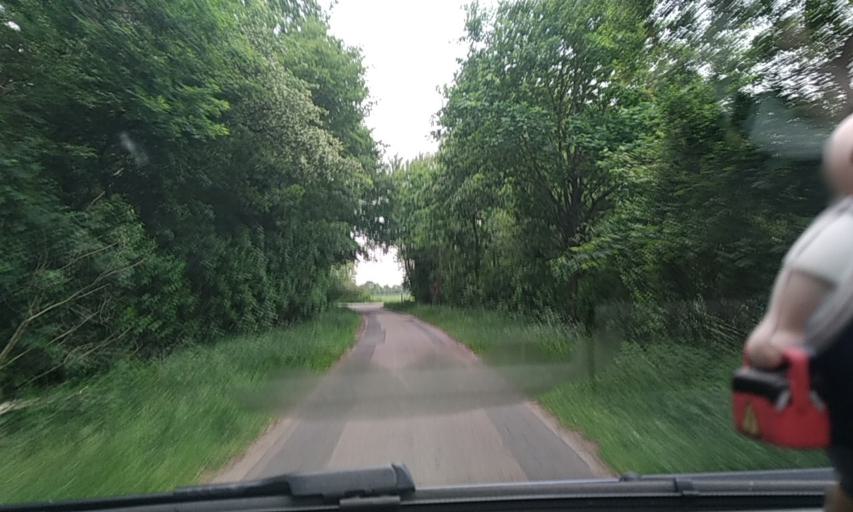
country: DE
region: Schleswig-Holstein
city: Borm
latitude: 54.3856
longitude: 9.3964
